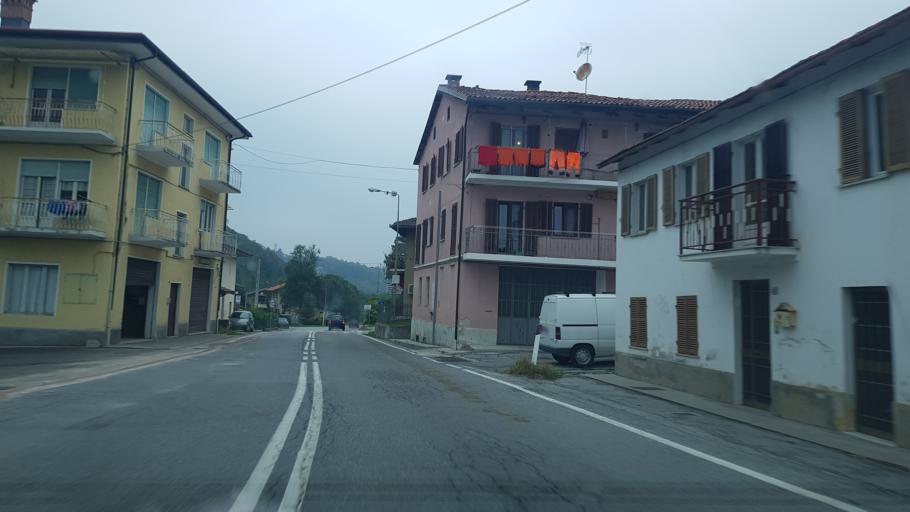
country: IT
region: Piedmont
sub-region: Provincia di Cuneo
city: Frabosa Sottana
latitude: 44.3271
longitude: 7.7943
